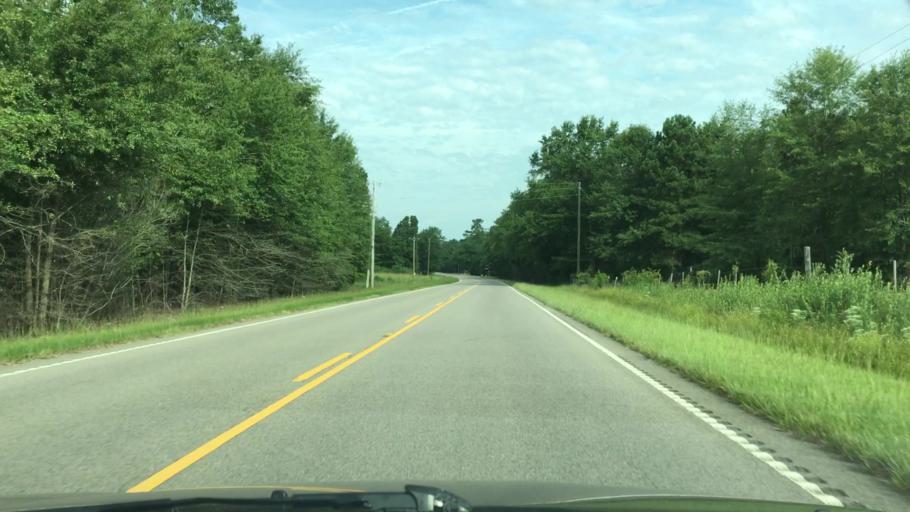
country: US
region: South Carolina
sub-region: Barnwell County
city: Williston
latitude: 33.6658
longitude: -81.3967
